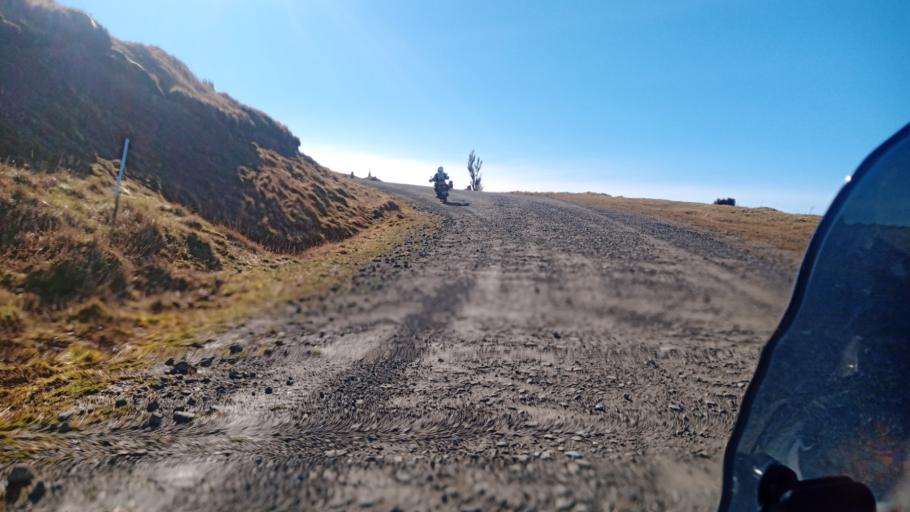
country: NZ
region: Gisborne
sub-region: Gisborne District
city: Gisborne
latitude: -38.1797
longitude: 177.8251
